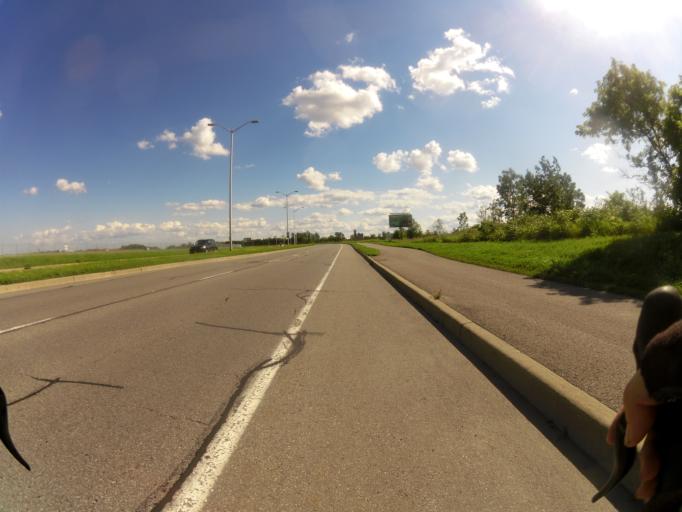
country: CA
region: Ontario
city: Ottawa
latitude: 45.3324
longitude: -75.6937
